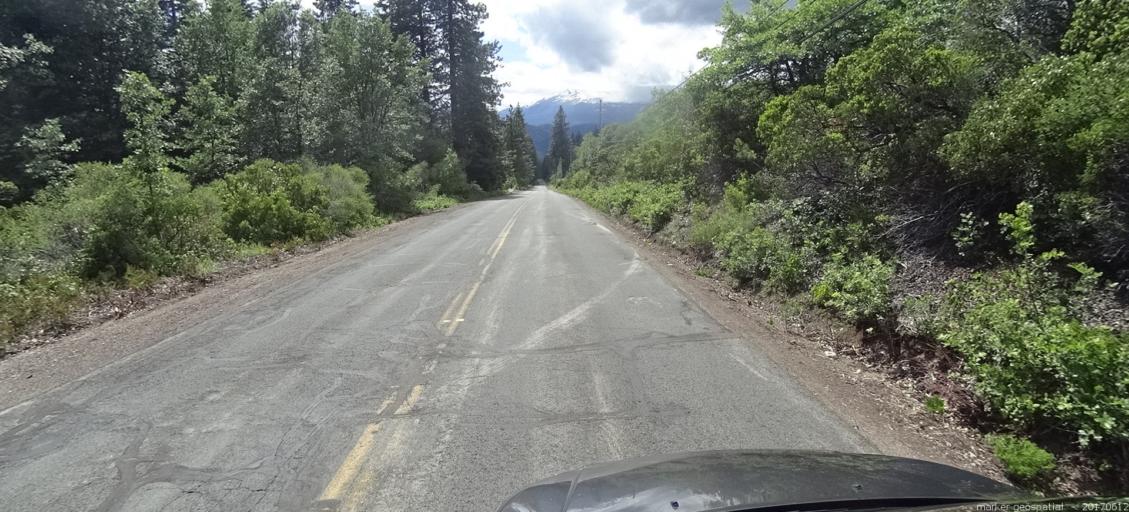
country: US
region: California
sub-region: Siskiyou County
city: Mount Shasta
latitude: 41.3122
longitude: -122.2904
